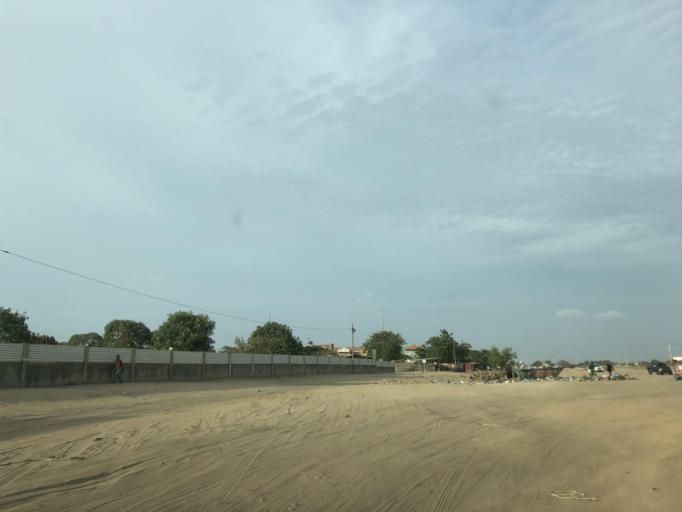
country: AO
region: Luanda
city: Luanda
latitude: -8.9149
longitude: 13.3120
